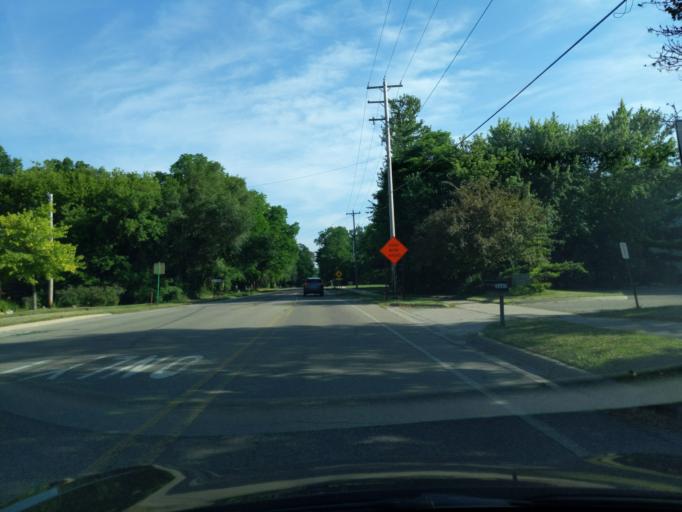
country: US
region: Michigan
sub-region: Ingham County
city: Okemos
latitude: 42.7464
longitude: -84.4277
